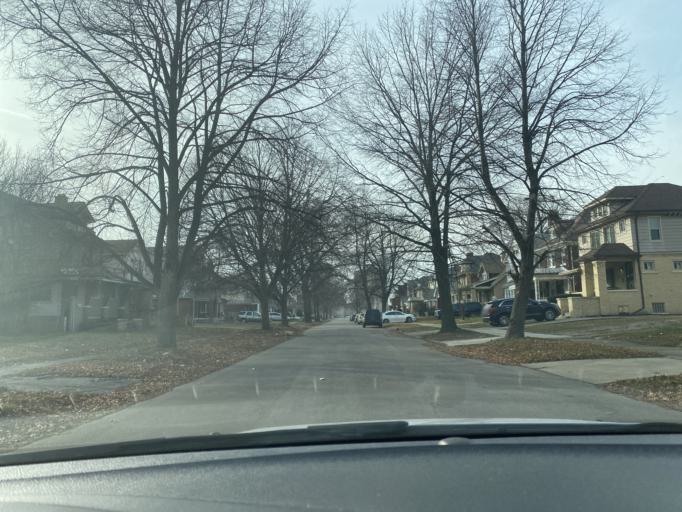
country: US
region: Michigan
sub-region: Wayne County
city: Highland Park
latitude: 42.3791
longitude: -83.1197
